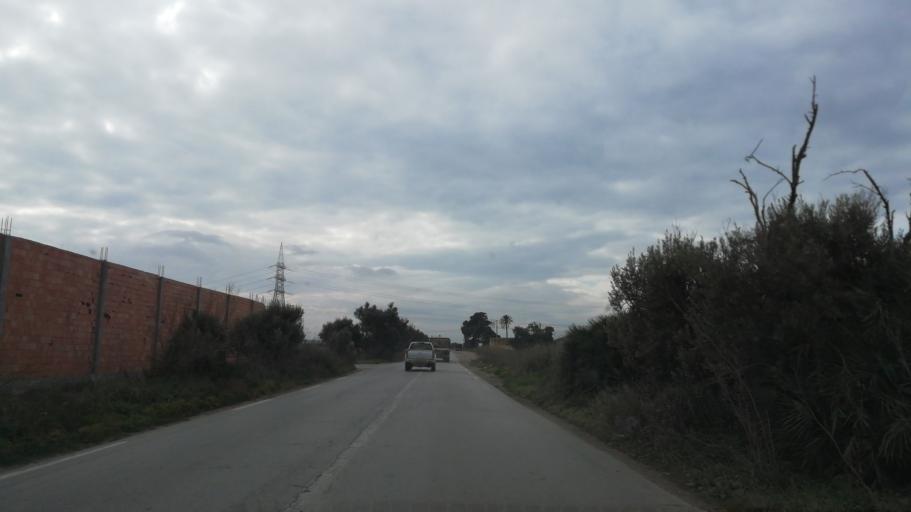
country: DZ
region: Oran
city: Ain el Bya
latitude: 35.7727
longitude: -0.3468
